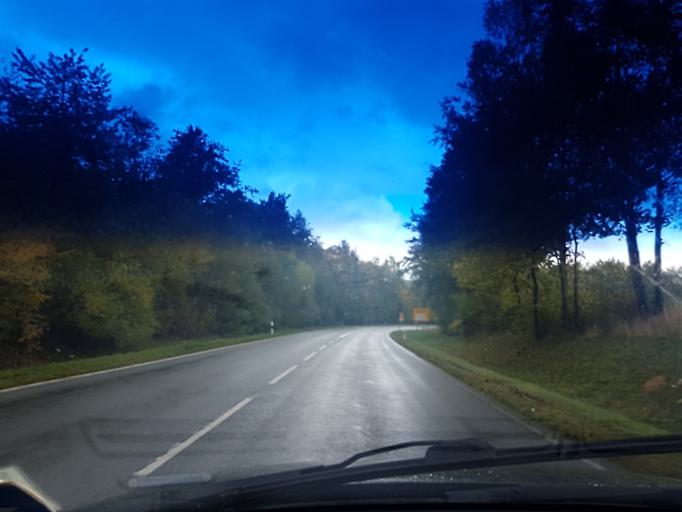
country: DE
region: Bavaria
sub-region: Upper Franconia
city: Bad Alexandersbad
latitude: 50.0229
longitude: 12.0144
